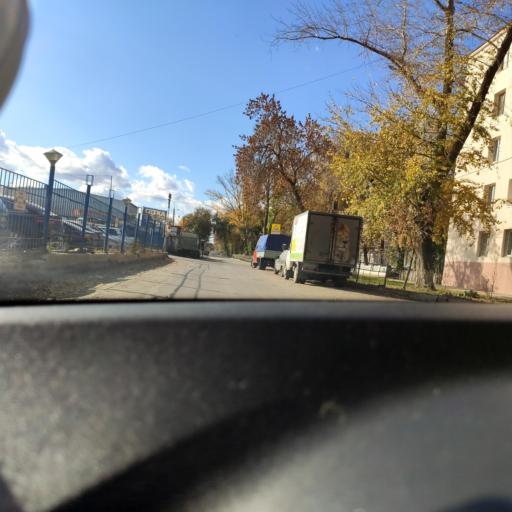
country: RU
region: Samara
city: Samara
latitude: 53.2093
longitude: 50.2511
